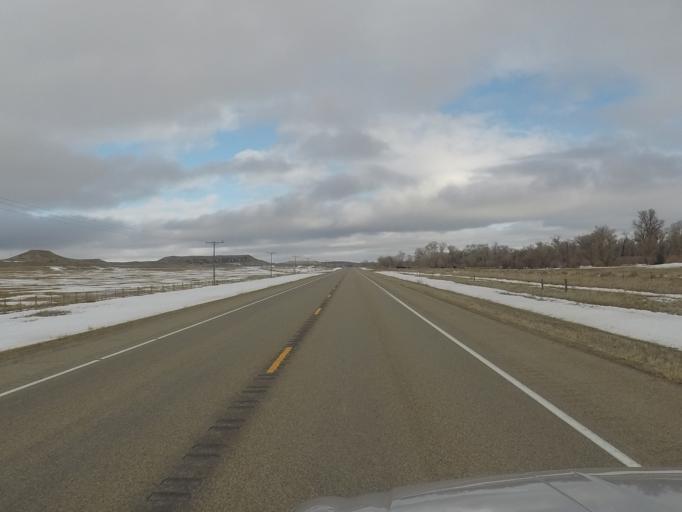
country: US
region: Montana
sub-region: Golden Valley County
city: Ryegate
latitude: 46.3188
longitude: -109.4189
